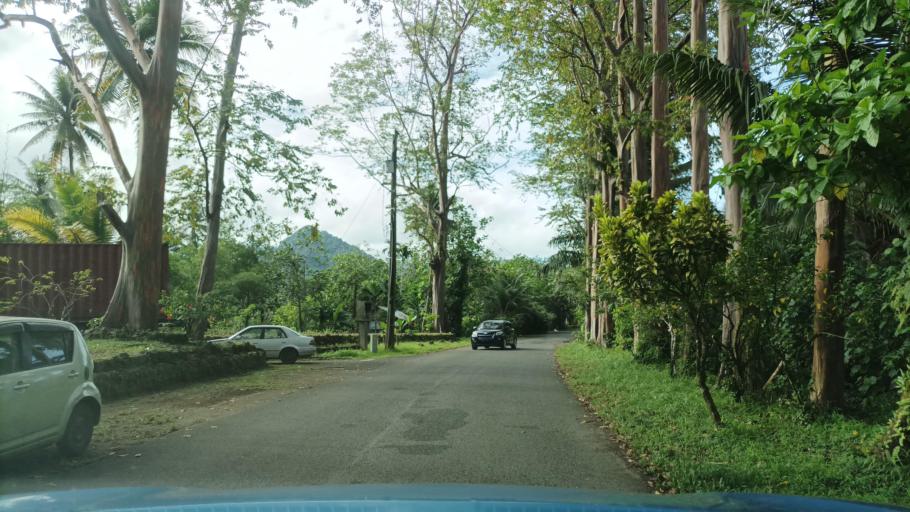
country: FM
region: Pohnpei
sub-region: Kolonia Municipality
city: Kolonia
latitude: 6.9412
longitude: 158.2249
